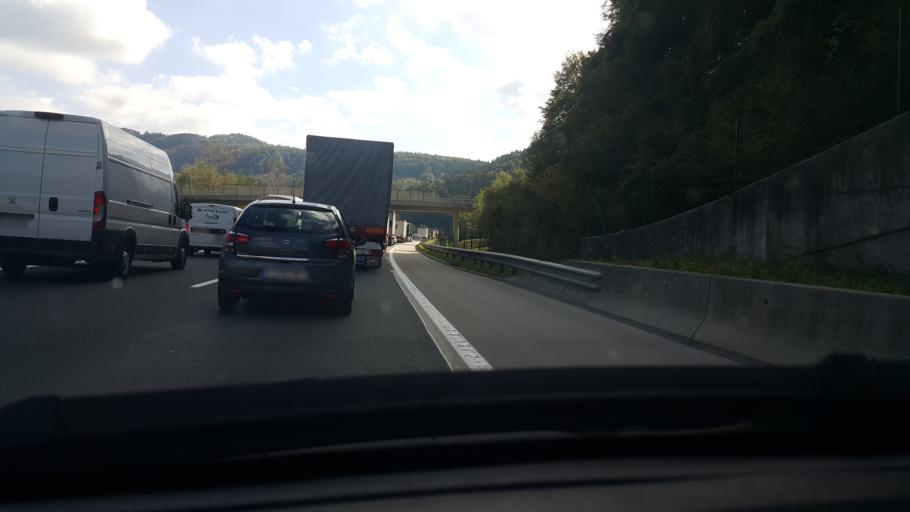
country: SI
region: Moravce
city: Moravce
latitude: 46.1685
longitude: 14.7373
